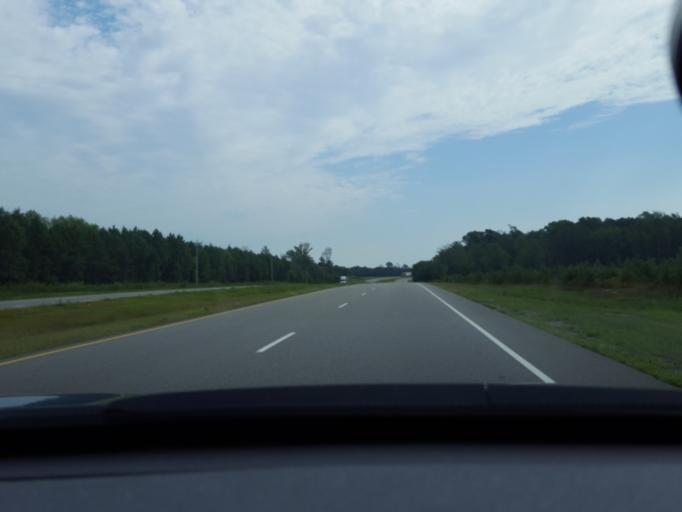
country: US
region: North Carolina
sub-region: Chowan County
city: Edenton
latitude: 36.0381
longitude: -76.7560
